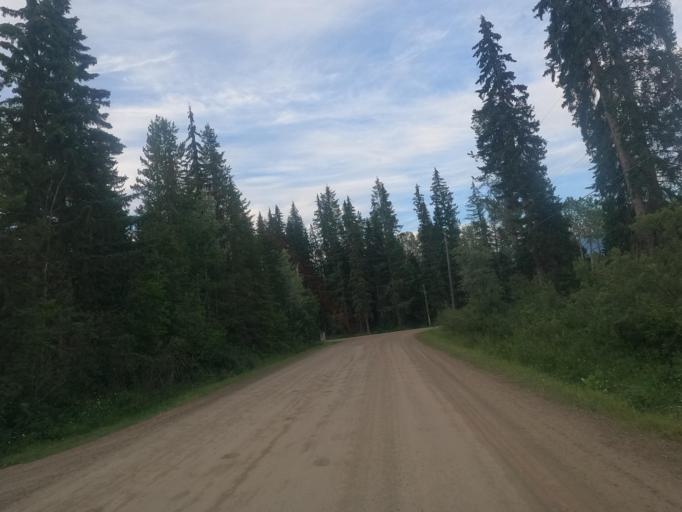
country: CA
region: British Columbia
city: Golden
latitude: 51.4390
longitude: -117.0414
